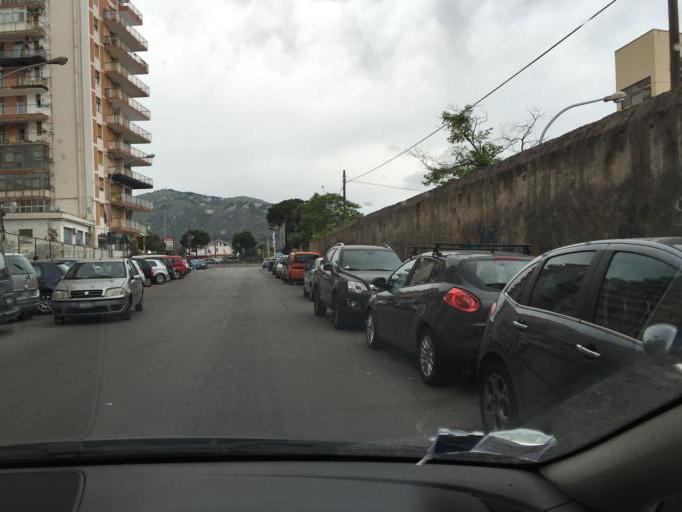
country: IT
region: Sicily
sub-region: Palermo
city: Palermo
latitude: 38.1068
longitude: 13.3315
